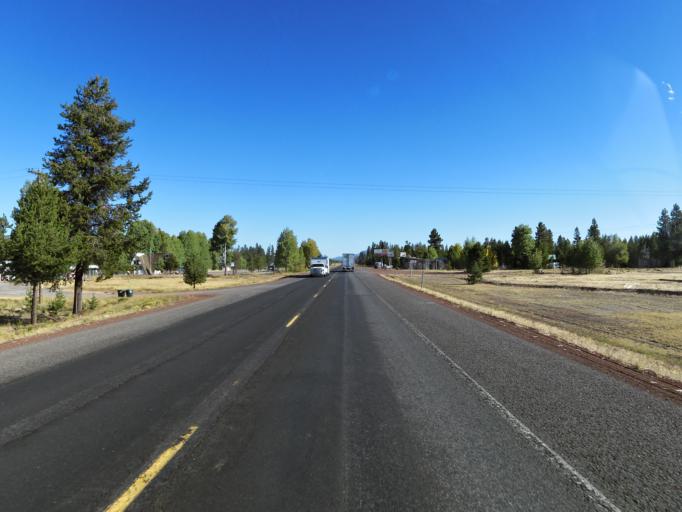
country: US
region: Oregon
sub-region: Deschutes County
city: La Pine
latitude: 43.1325
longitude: -121.8037
